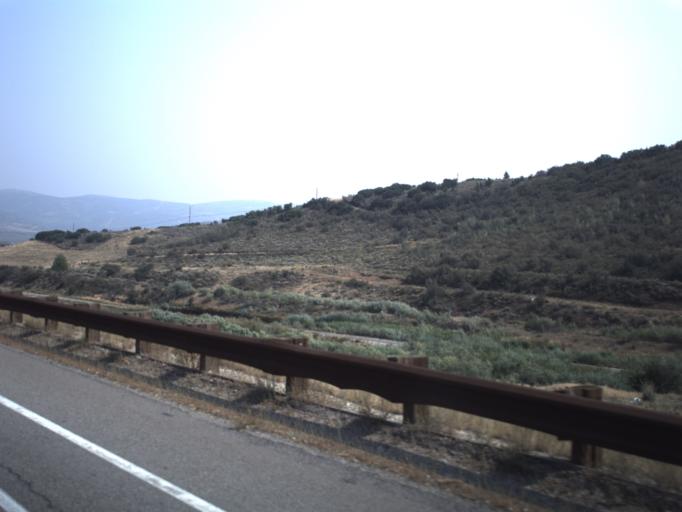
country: US
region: Utah
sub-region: Summit County
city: Park City
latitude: 40.6719
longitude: -111.4727
